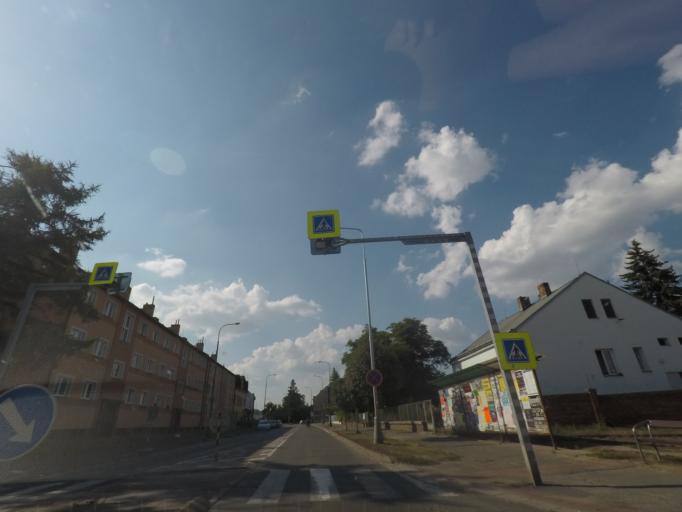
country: CZ
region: Kralovehradecky
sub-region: Okres Nachod
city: Jaromer
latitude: 50.3475
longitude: 15.9149
